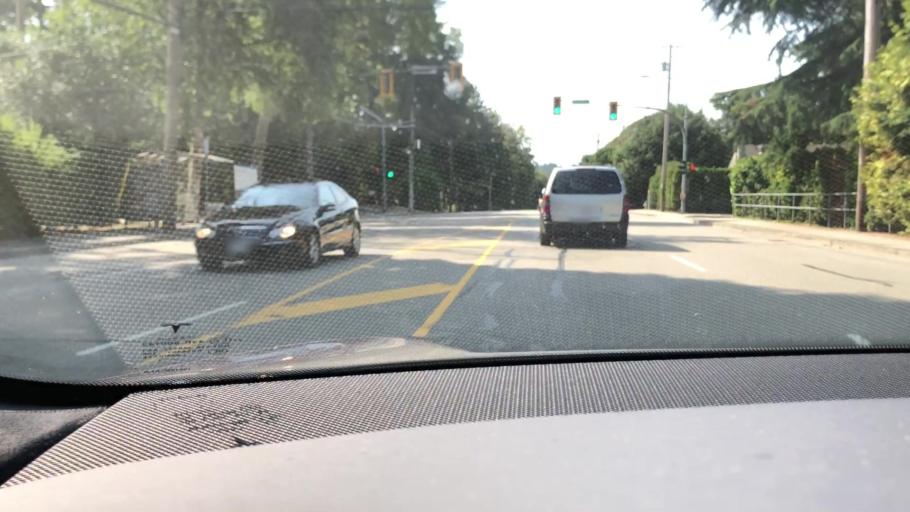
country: US
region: Washington
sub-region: Whatcom County
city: Point Roberts
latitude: 49.0184
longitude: -123.0687
